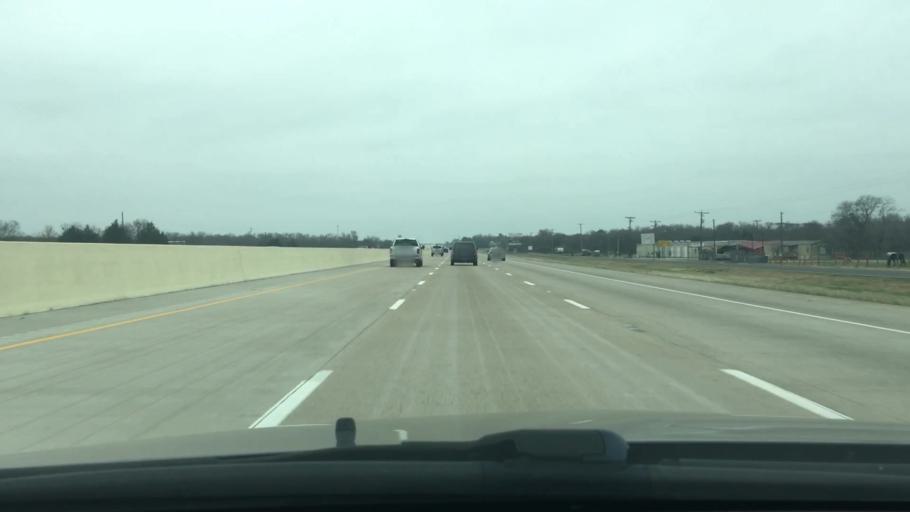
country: US
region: Texas
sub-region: Navarro County
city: Corsicana
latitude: 32.0245
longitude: -96.4406
